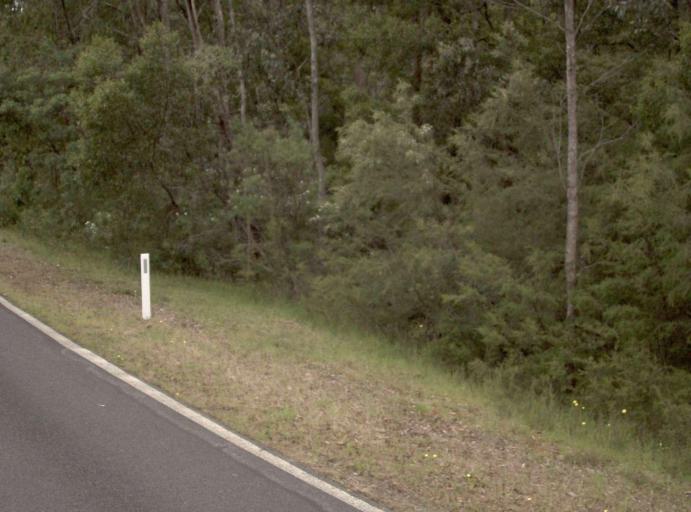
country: AU
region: Victoria
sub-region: East Gippsland
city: Bairnsdale
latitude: -37.6433
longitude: 147.2728
